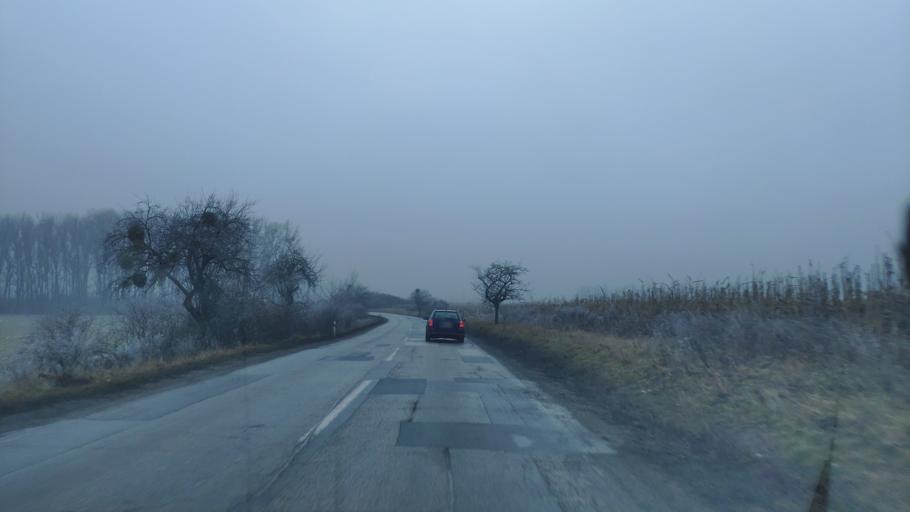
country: SK
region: Kosicky
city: Kosice
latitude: 48.6602
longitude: 21.2767
